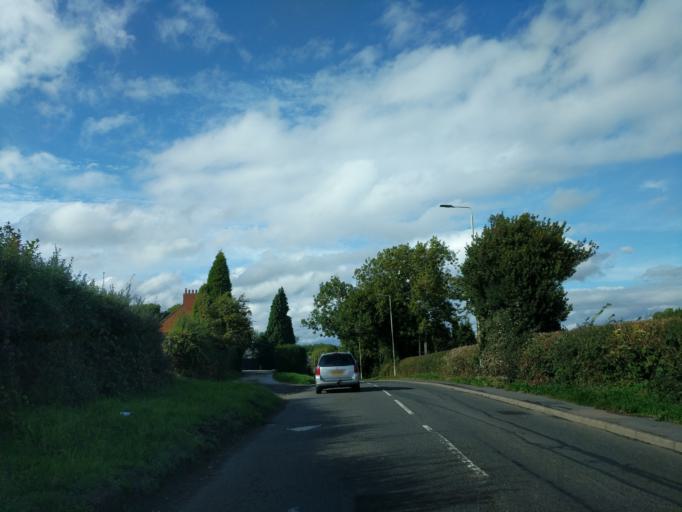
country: GB
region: England
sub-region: Leicestershire
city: Coalville
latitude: 52.7034
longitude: -1.3714
